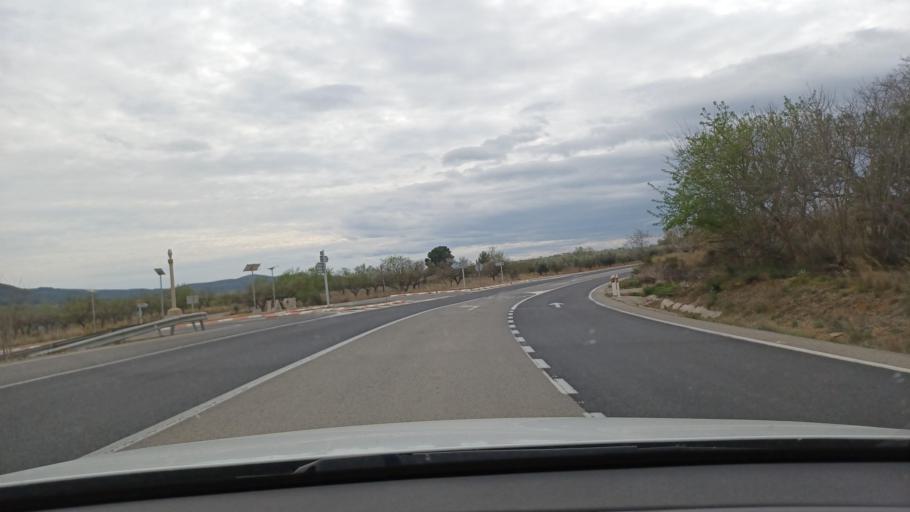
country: ES
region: Catalonia
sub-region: Provincia de Tarragona
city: Santa Barbara
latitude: 40.6786
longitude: 0.4582
